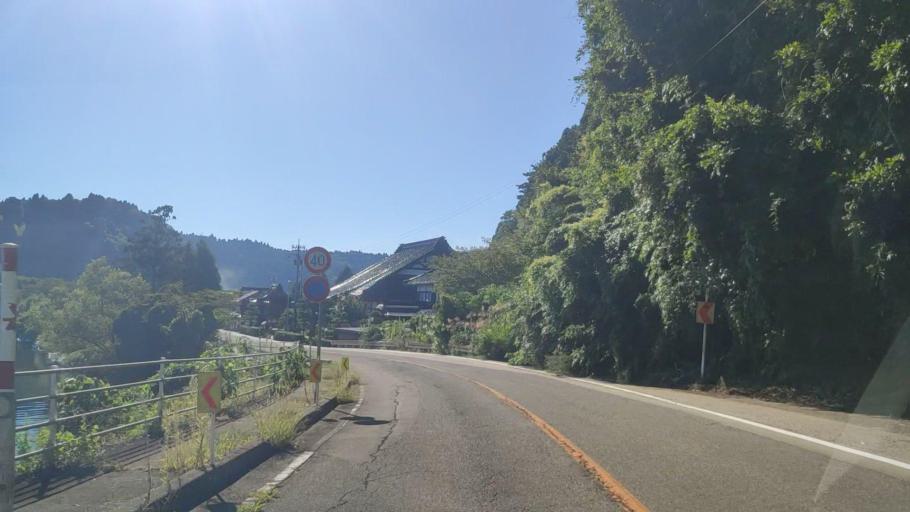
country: JP
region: Ishikawa
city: Nanao
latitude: 37.2570
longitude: 137.0855
